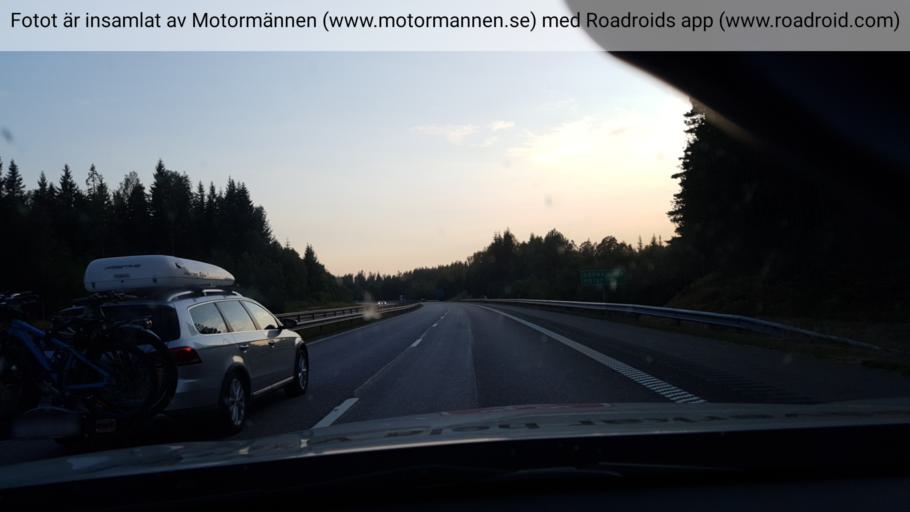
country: SE
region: Vaestra Goetaland
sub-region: Bollebygds Kommun
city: Bollebygd
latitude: 57.6711
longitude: 12.6254
